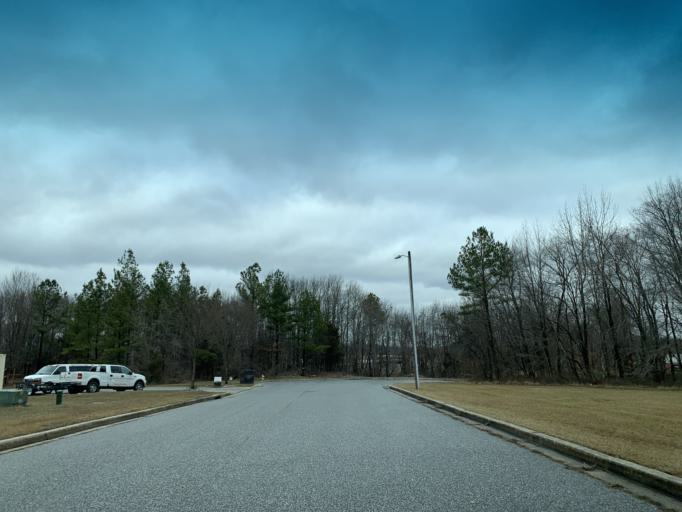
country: US
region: Maryland
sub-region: Harford County
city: Edgewood
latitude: 39.4331
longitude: -76.3080
